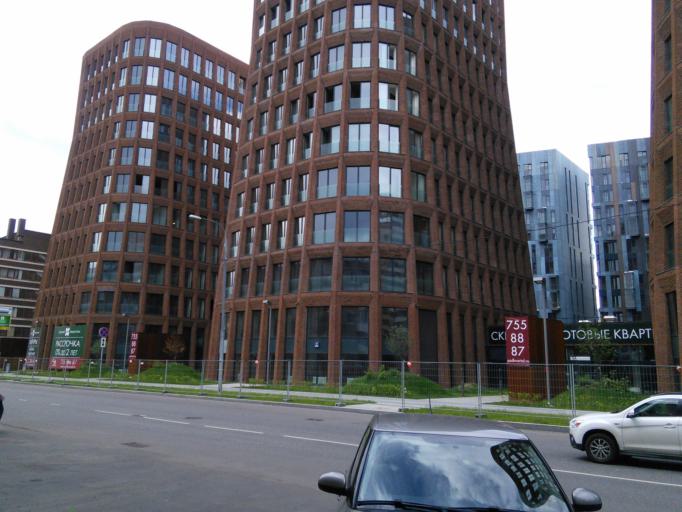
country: RU
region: Moscow
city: Luzhniki
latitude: 55.7259
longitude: 37.5756
